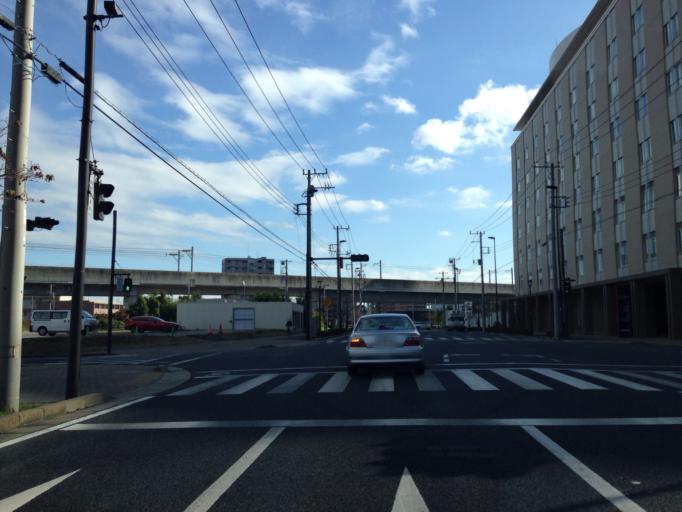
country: JP
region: Chiba
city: Kashiwa
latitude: 35.8969
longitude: 139.9521
